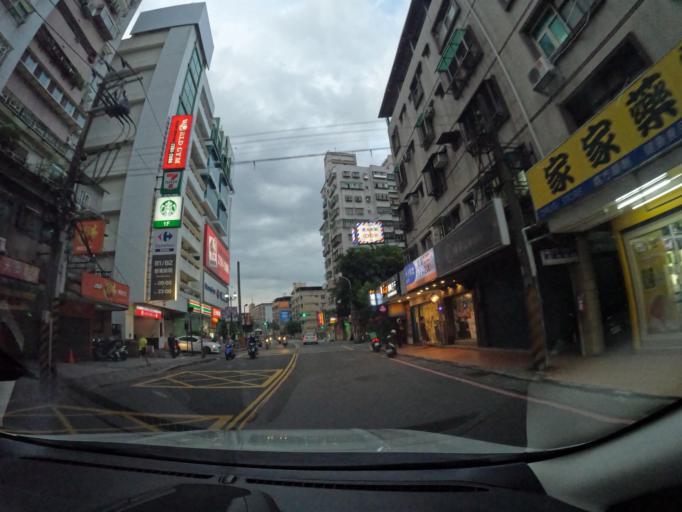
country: TW
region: Taipei
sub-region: Taipei
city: Banqiao
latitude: 24.9829
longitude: 121.4592
